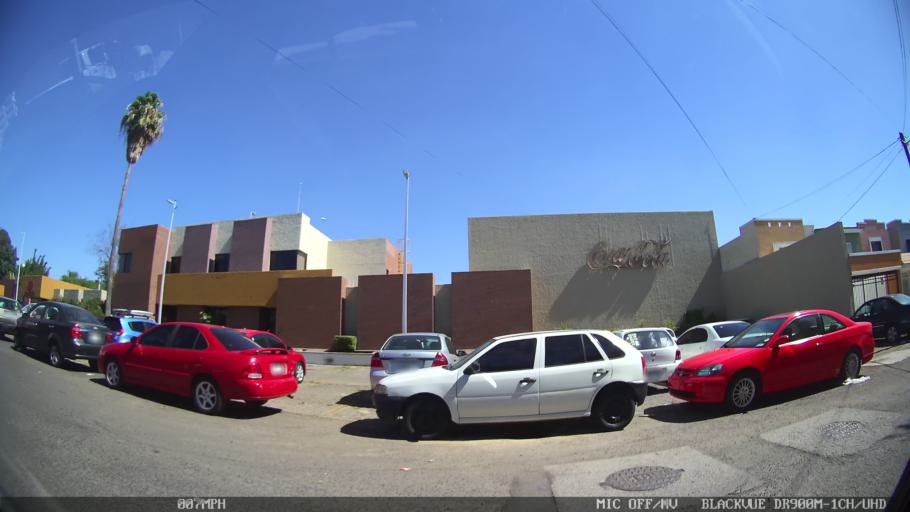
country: MX
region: Jalisco
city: Tlaquepaque
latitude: 20.6513
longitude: -103.2916
